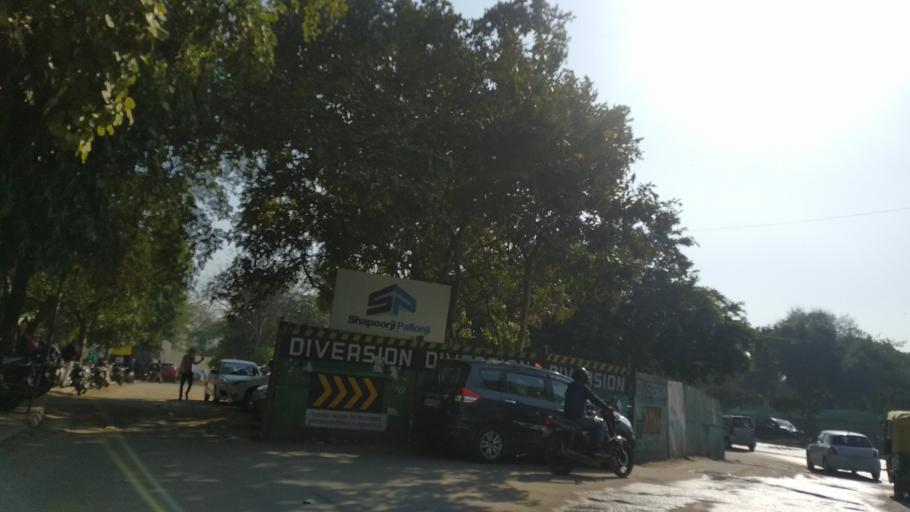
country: IN
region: NCT
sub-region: New Delhi
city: New Delhi
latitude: 28.6187
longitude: 77.2407
